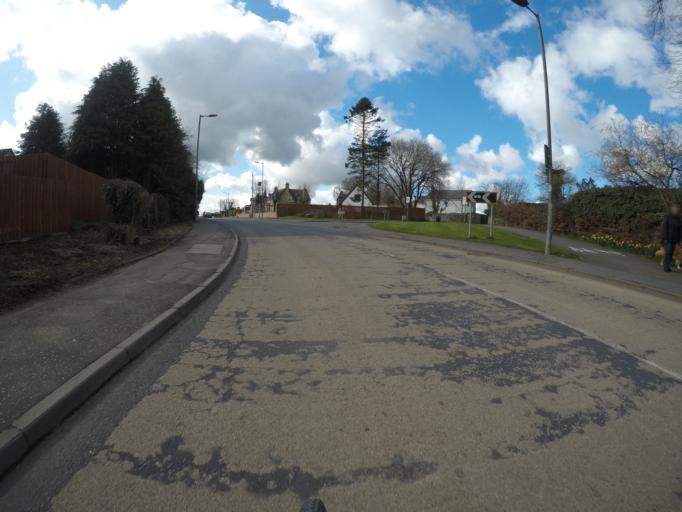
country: GB
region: Scotland
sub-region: North Ayrshire
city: Beith
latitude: 55.7461
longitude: -4.6402
